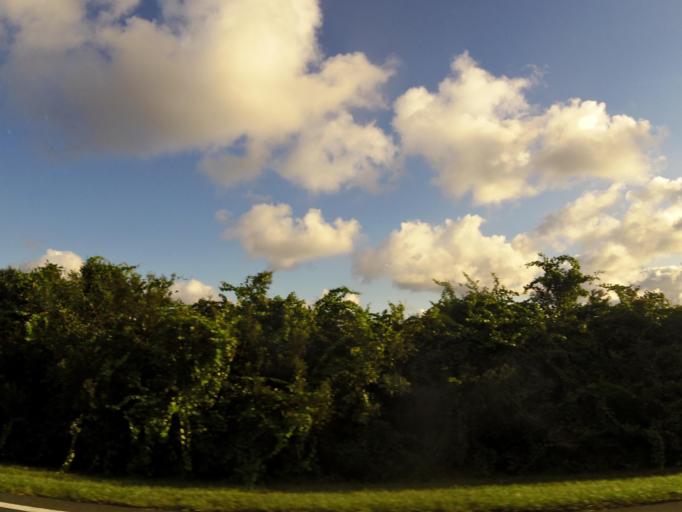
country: US
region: Georgia
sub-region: Glynn County
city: Saint Simon Mills
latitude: 31.1862
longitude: -81.3916
